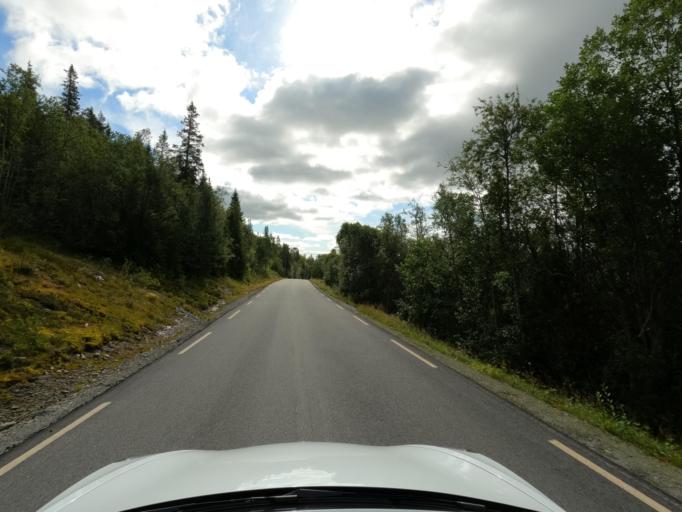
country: NO
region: Telemark
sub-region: Tinn
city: Rjukan
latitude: 60.1449
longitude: 8.6351
